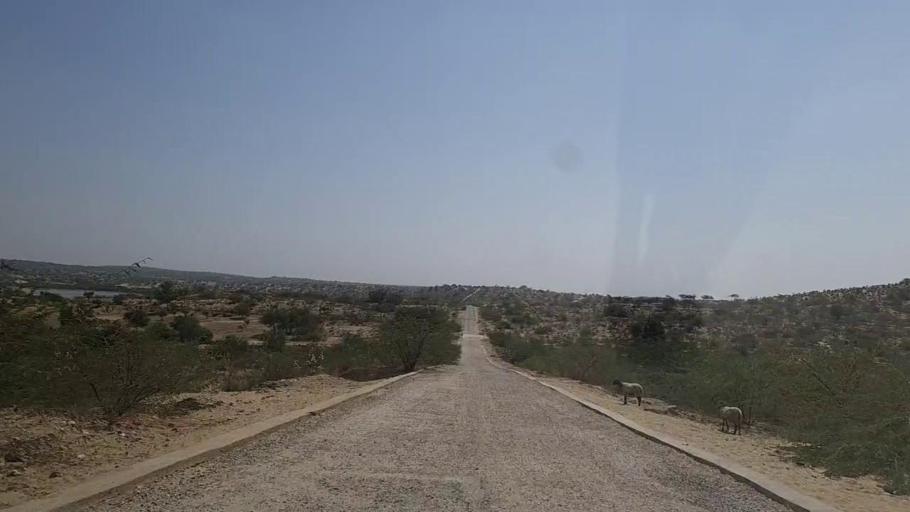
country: PK
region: Sindh
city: Diplo
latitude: 24.5204
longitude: 69.3598
